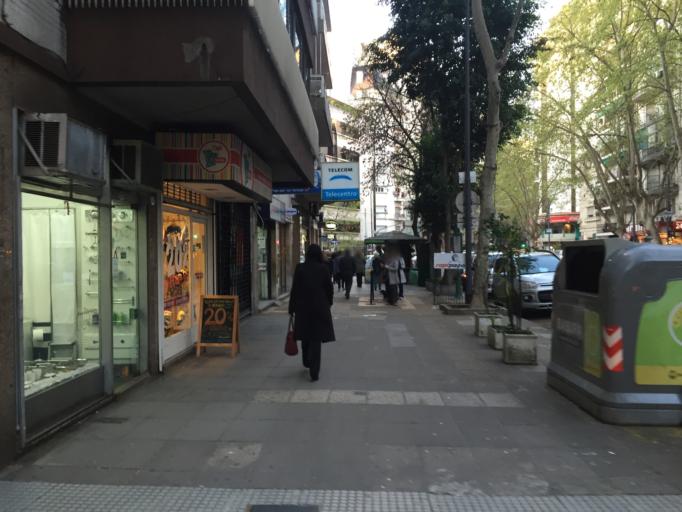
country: AR
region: Buenos Aires F.D.
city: Retiro
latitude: -34.5899
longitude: -58.4000
